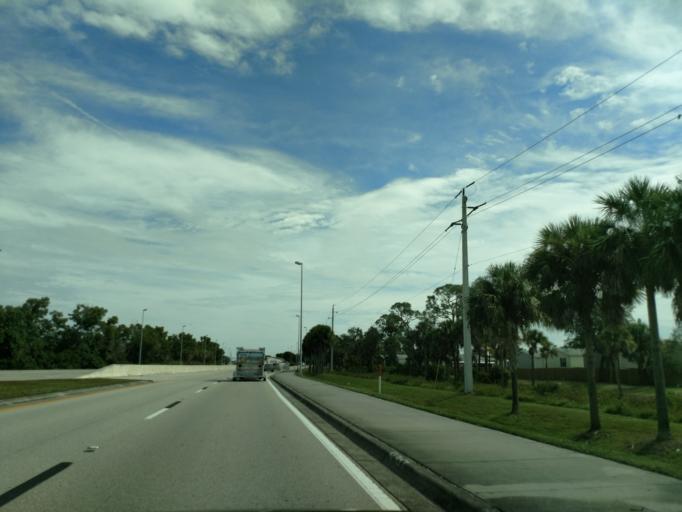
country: US
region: Florida
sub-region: Lee County
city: Iona
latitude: 26.4941
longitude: -81.9495
